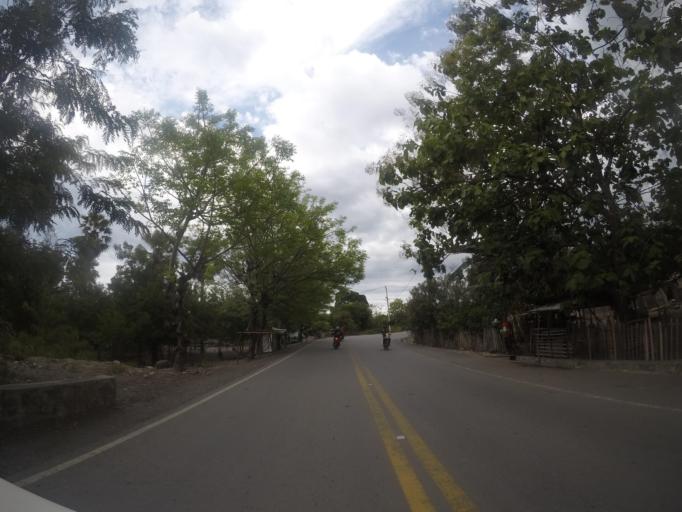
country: TL
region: Liquica
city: Liquica
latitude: -8.5904
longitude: 125.3304
